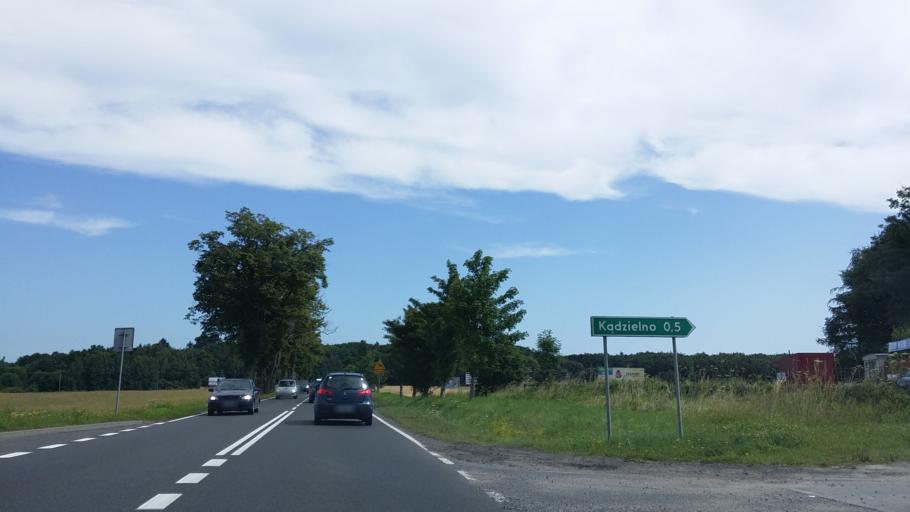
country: PL
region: West Pomeranian Voivodeship
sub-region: Powiat kolobrzeski
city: Kolobrzeg
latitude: 54.1817
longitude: 15.6333
